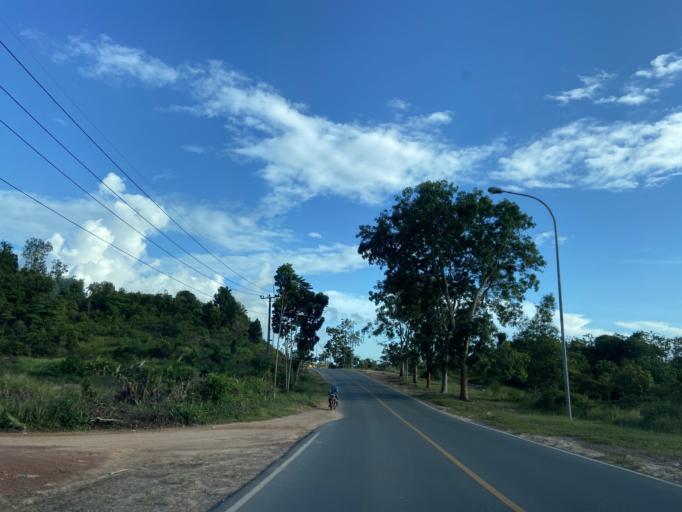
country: SG
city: Singapore
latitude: 0.9968
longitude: 104.0321
